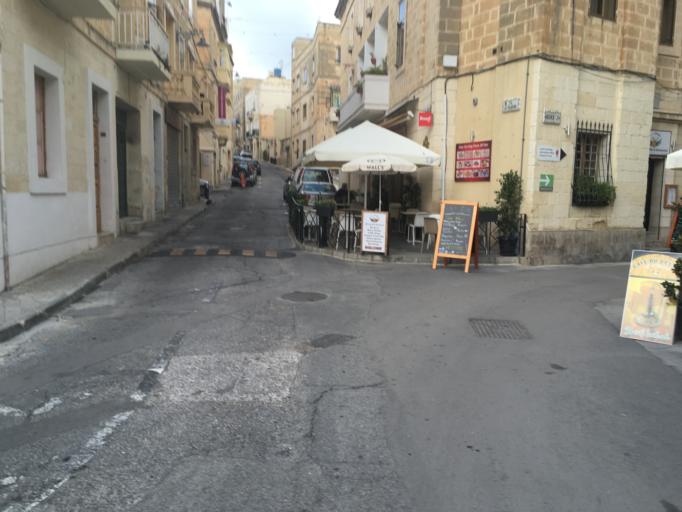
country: MT
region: L-Isla
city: Senglea
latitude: 35.8882
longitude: 14.5222
